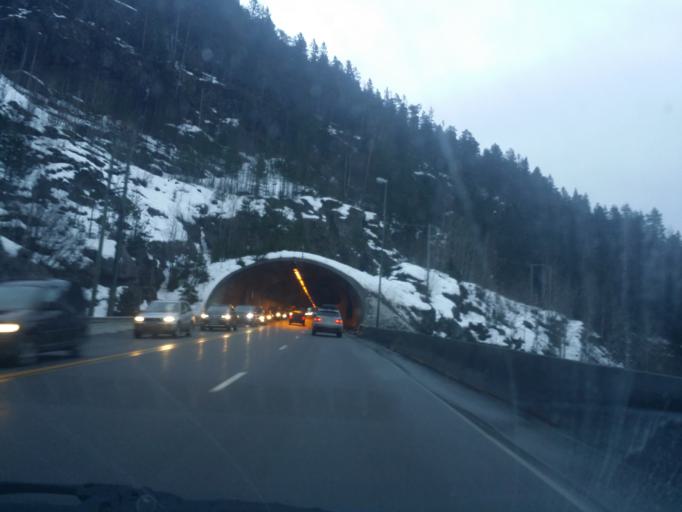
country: NO
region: Buskerud
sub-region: Hole
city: Vik
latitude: 59.9813
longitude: 10.3127
